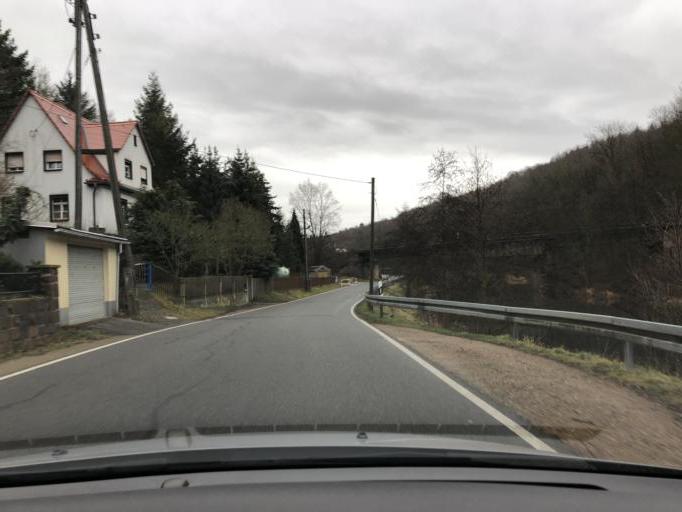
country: DE
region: Saxony
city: Rosswein
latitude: 51.0690
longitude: 13.2028
